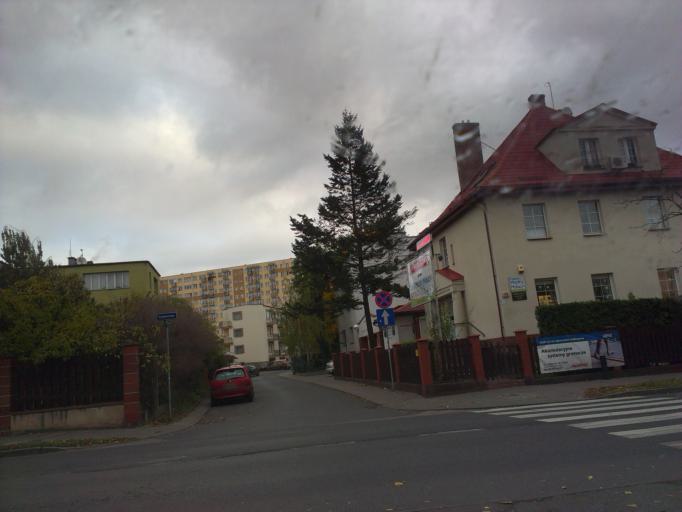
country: PL
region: Kujawsko-Pomorskie
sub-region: Torun
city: Torun
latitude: 53.0187
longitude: 18.6028
